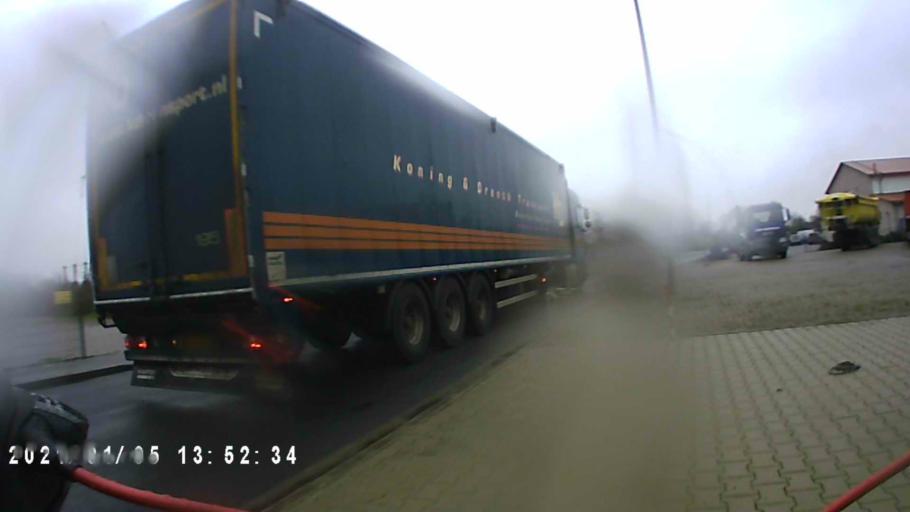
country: DE
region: Lower Saxony
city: Weener
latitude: 53.1732
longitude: 7.3588
